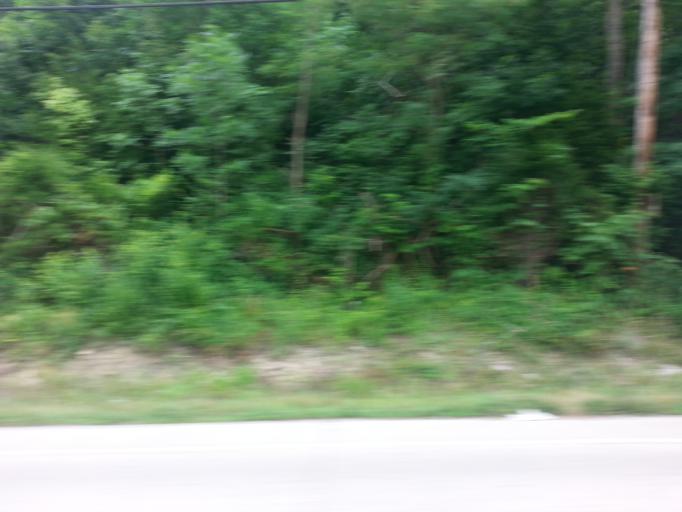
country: US
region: Ohio
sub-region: Brown County
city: Aberdeen
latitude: 38.7055
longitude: -83.7974
